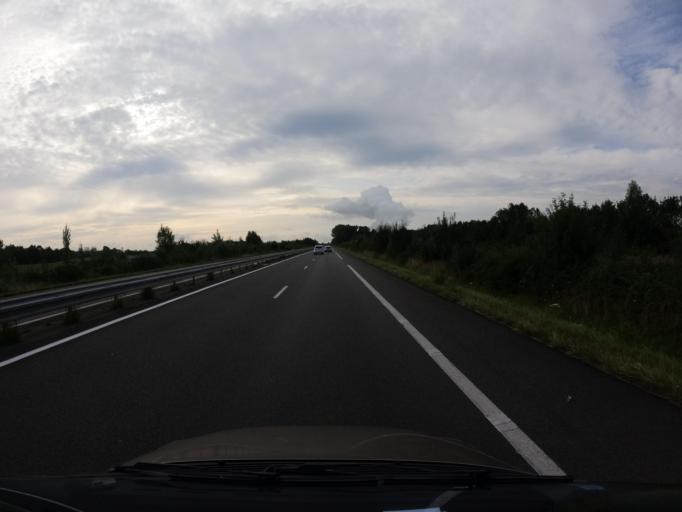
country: FR
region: Centre
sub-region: Departement d'Indre-et-Loire
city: Saint-Nicolas-de-Bourgueil
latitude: 47.2707
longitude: 0.1117
